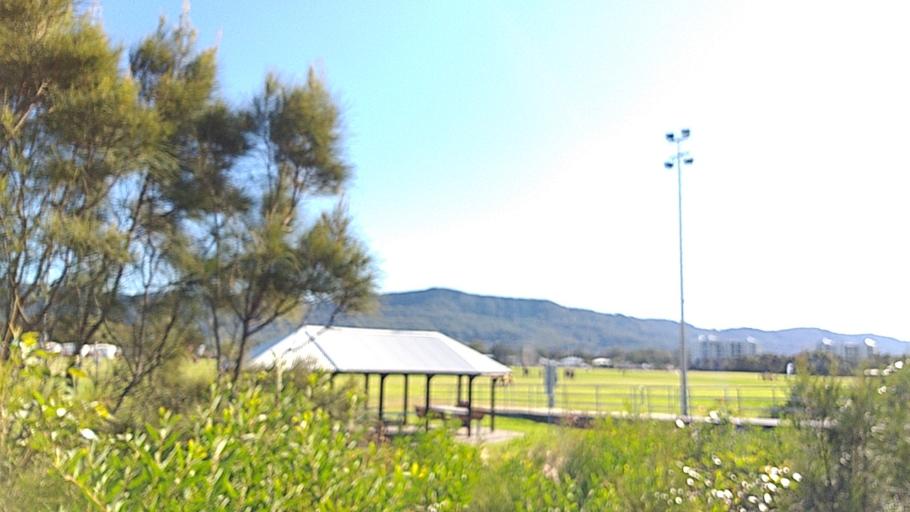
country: AU
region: New South Wales
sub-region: Wollongong
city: Fairy Meadow
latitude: -34.3957
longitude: 150.9045
